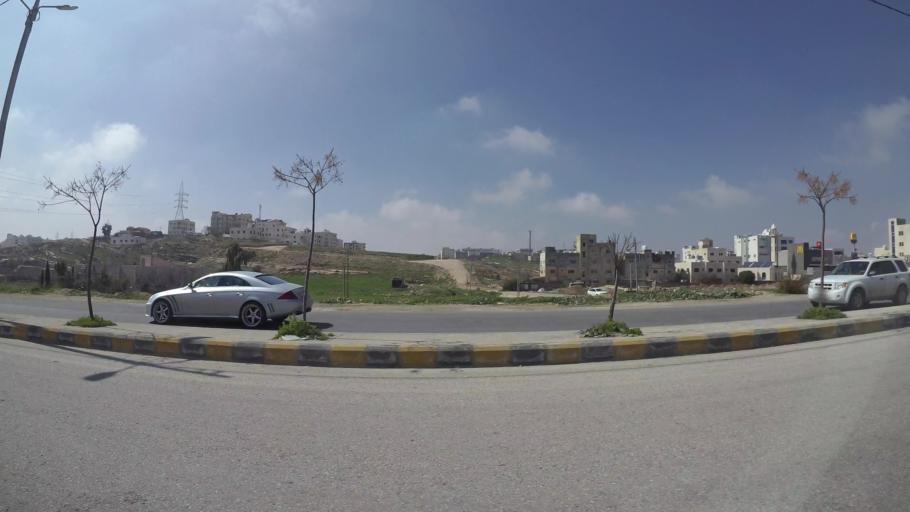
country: JO
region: Amman
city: Al Bunayyat ash Shamaliyah
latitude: 31.8947
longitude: 35.9038
